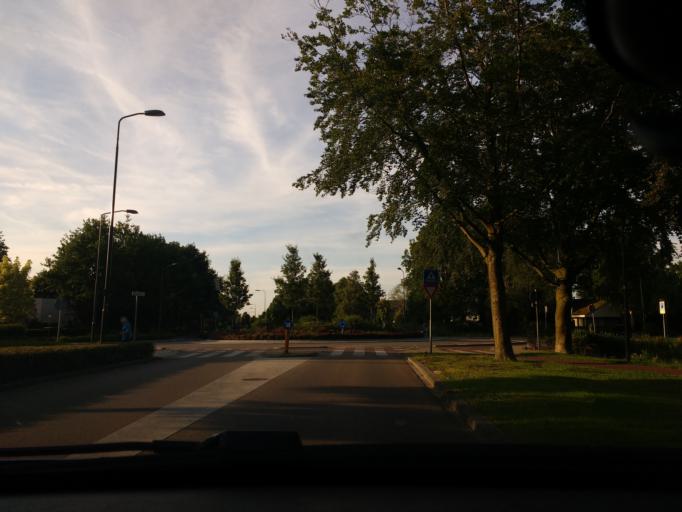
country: NL
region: Utrecht
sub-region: Gemeente Veenendaal
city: Veenendaal
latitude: 52.0278
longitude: 5.5643
